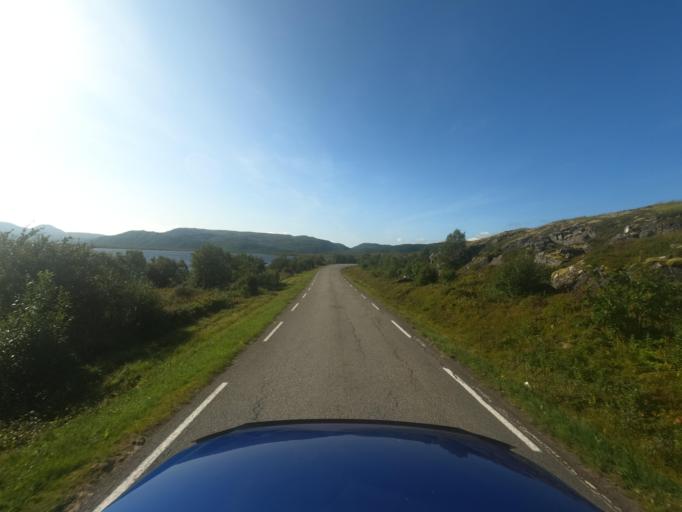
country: NO
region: Nordland
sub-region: Vestvagoy
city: Evjen
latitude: 68.3153
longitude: 13.8968
